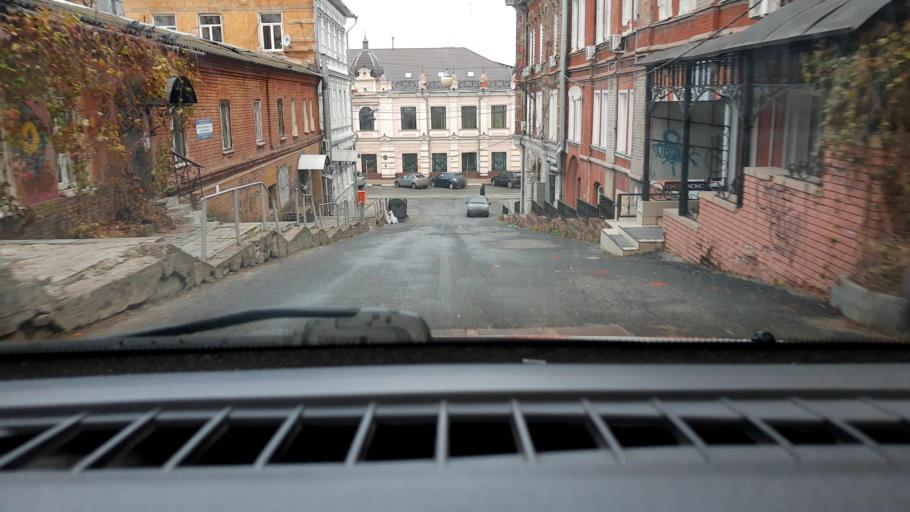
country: RU
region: Nizjnij Novgorod
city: Nizhniy Novgorod
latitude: 56.3276
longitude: 43.9879
